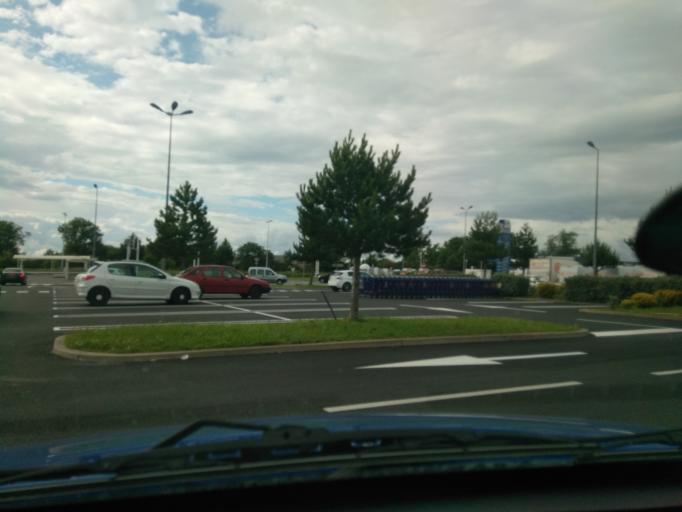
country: FR
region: Midi-Pyrenees
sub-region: Departement de l'Aveyron
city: Sebazac-Concoures
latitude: 44.3934
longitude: 2.6029
